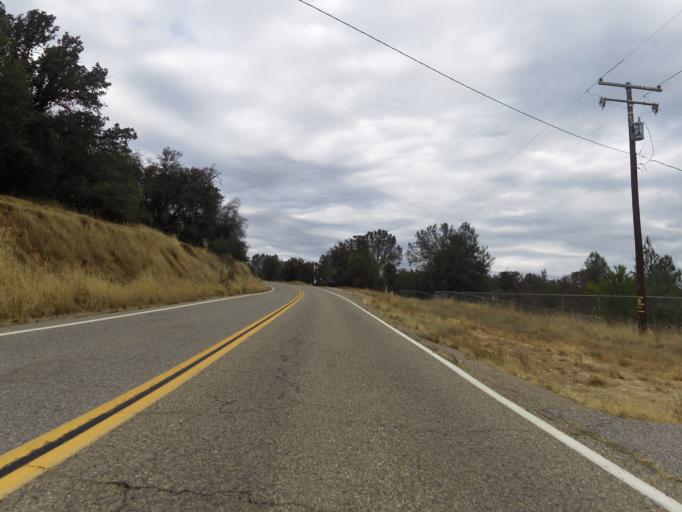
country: US
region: California
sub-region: Madera County
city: Yosemite Lakes
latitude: 37.2379
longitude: -119.7754
